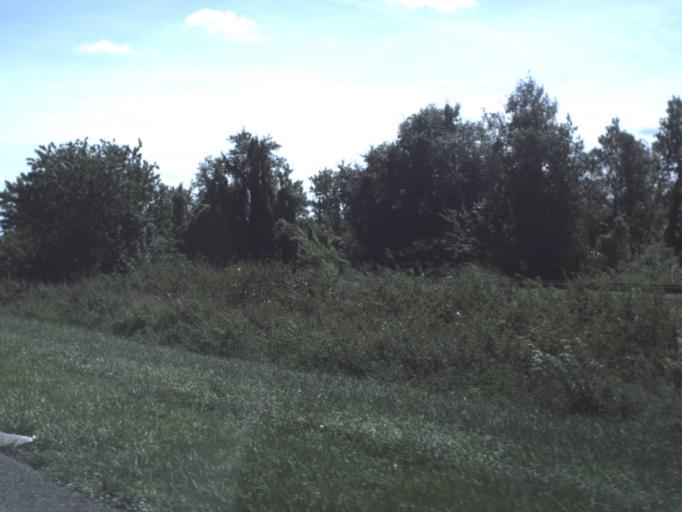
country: US
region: Florida
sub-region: Hendry County
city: Port LaBelle
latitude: 26.9235
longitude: -81.3082
